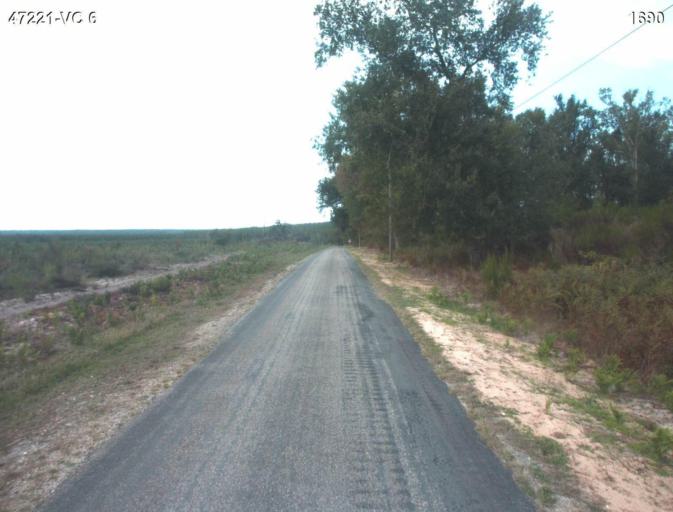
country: FR
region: Aquitaine
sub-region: Departement du Lot-et-Garonne
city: Mezin
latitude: 44.1044
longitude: 0.1615
